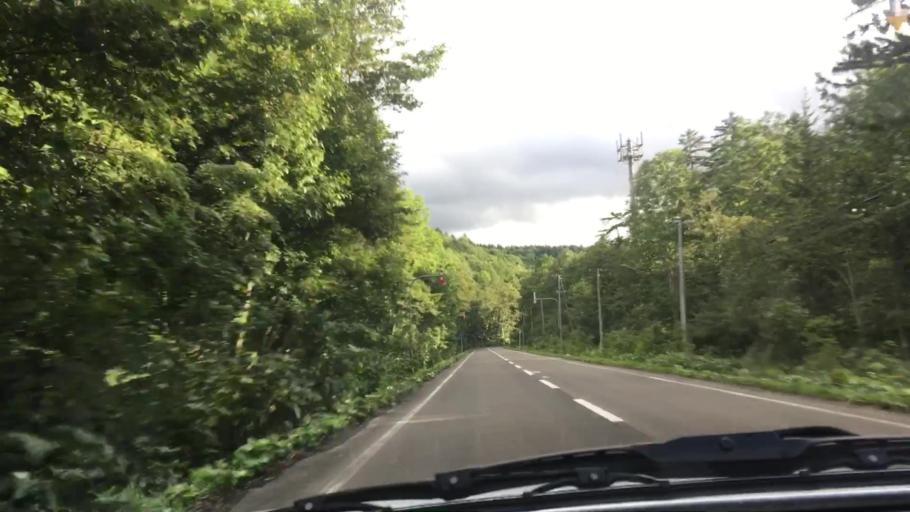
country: JP
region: Hokkaido
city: Shimo-furano
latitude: 43.0963
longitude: 142.6861
